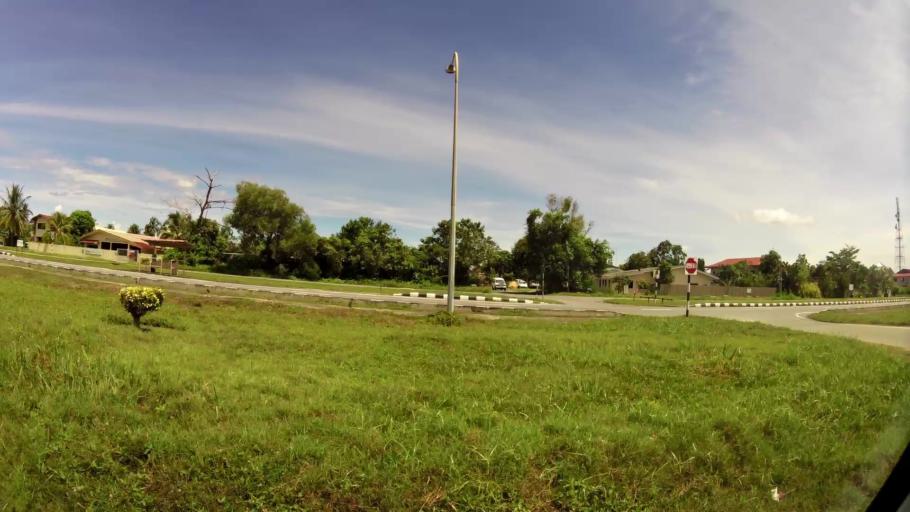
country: BN
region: Belait
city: Kuala Belait
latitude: 4.5937
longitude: 114.2349
